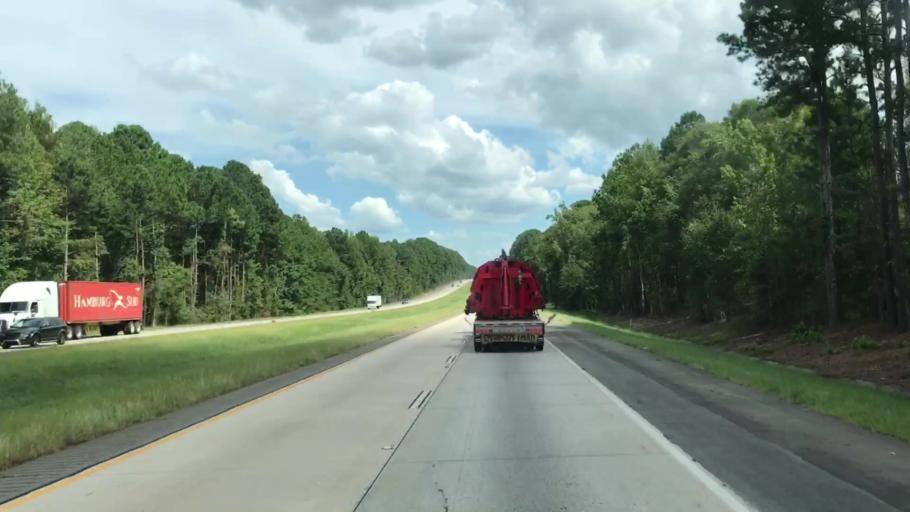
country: US
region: Georgia
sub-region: Greene County
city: Greensboro
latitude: 33.5492
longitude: -83.1311
